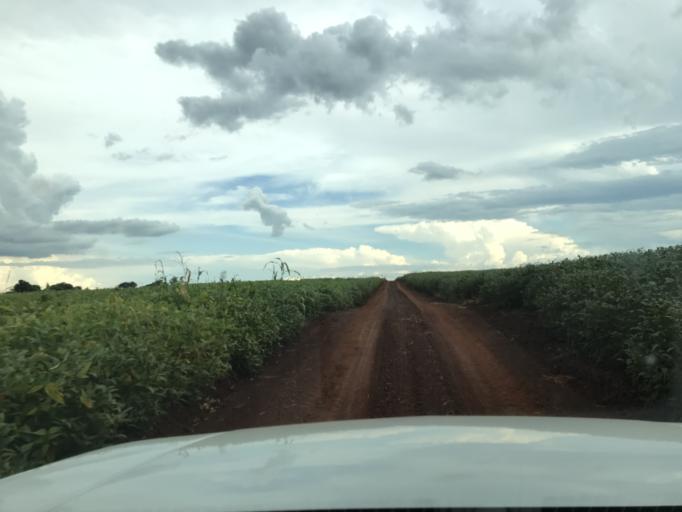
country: BR
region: Parana
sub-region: Palotina
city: Palotina
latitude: -24.2701
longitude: -53.7689
